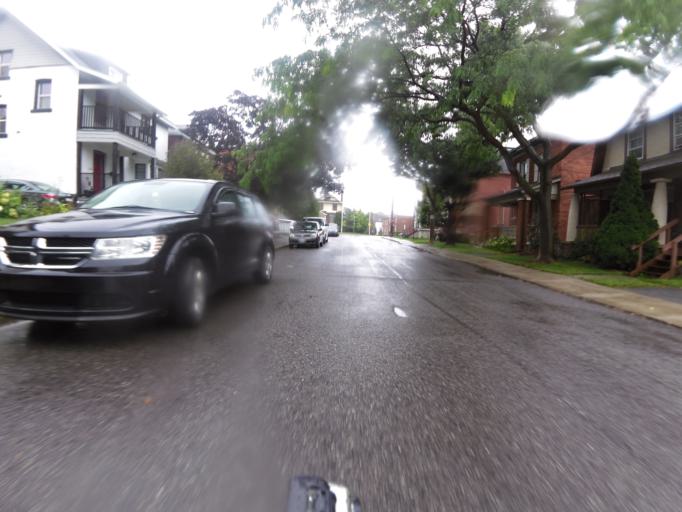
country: CA
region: Ontario
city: Ottawa
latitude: 45.4128
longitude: -75.6764
